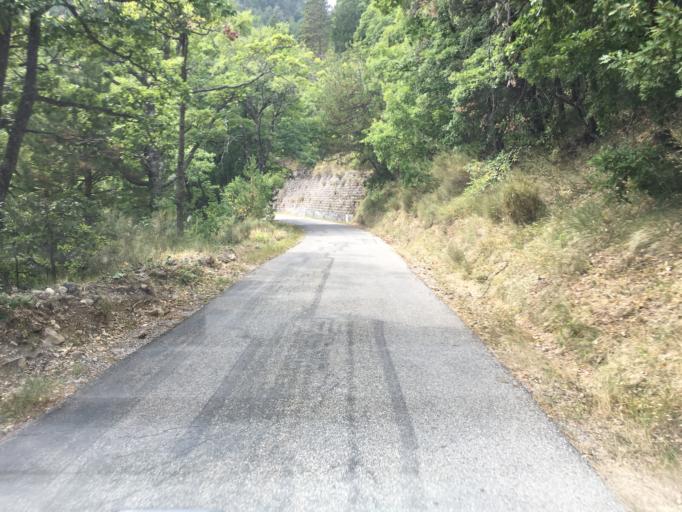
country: FR
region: Provence-Alpes-Cote d'Azur
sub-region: Departement des Alpes-de-Haute-Provence
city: Digne-les-Bains
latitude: 44.2046
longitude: 6.1496
